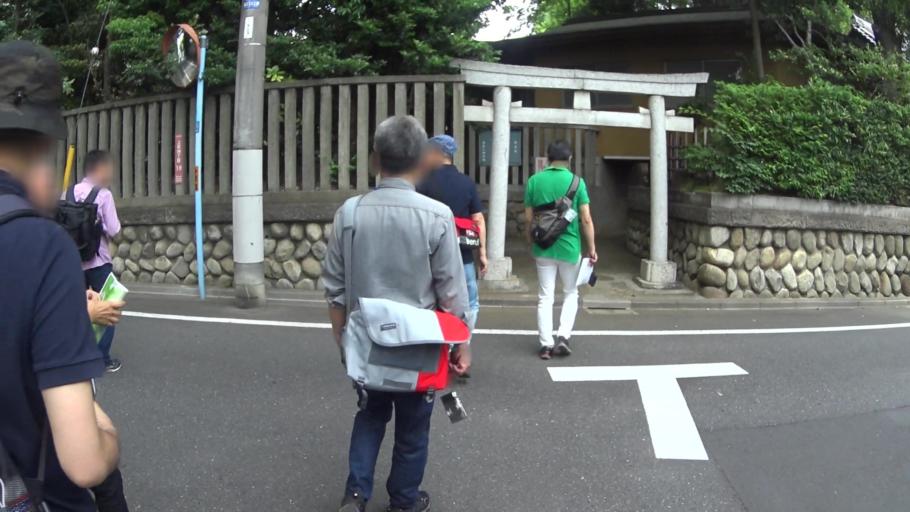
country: JP
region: Tokyo
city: Musashino
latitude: 35.7102
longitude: 139.6066
